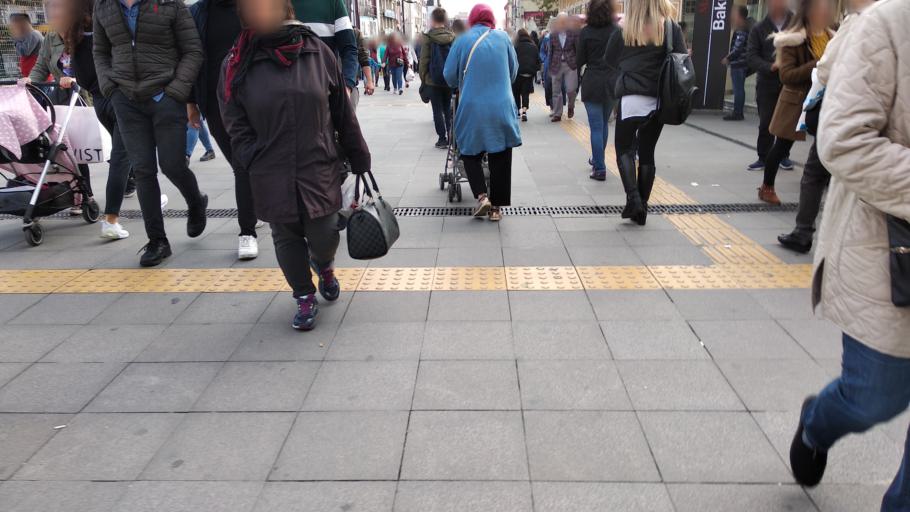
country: TR
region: Istanbul
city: Bahcelievler
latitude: 40.9807
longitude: 28.8738
